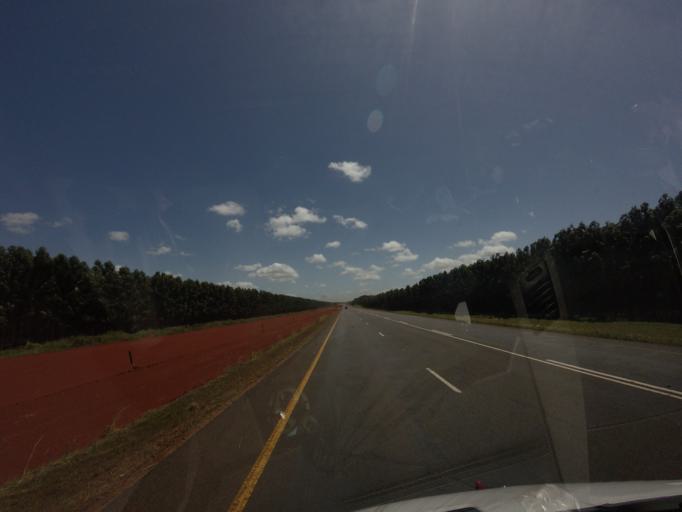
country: ZA
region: KwaZulu-Natal
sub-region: uThungulu District Municipality
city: Empangeni
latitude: -28.7597
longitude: 31.9335
